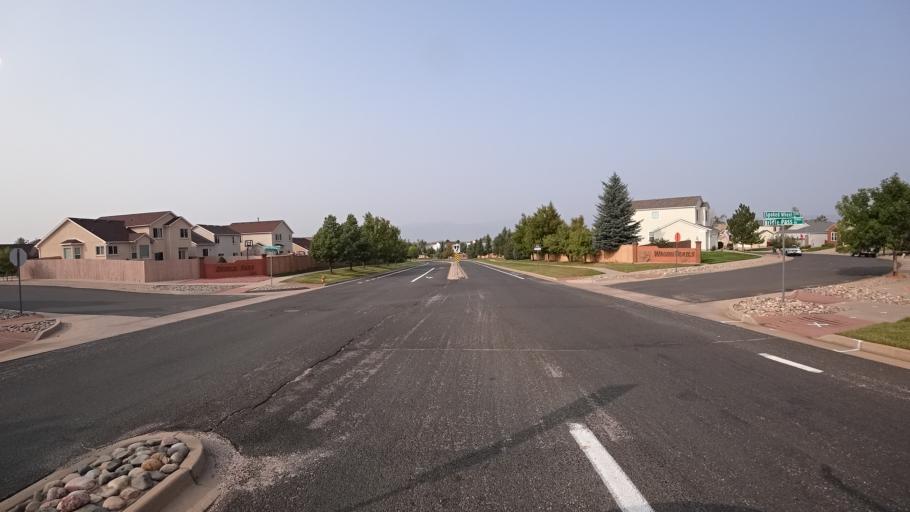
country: US
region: Colorado
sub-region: El Paso County
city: Cimarron Hills
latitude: 38.9316
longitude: -104.7262
